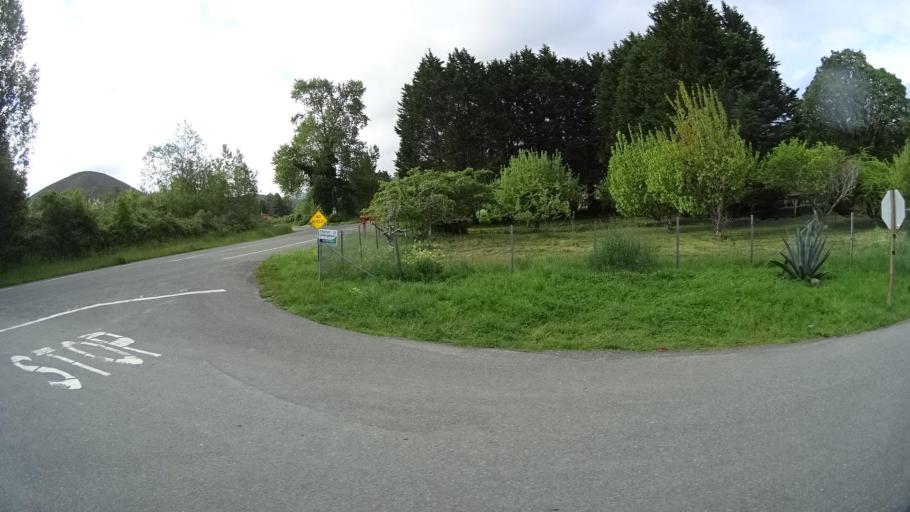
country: US
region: California
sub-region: Humboldt County
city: Blue Lake
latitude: 40.8682
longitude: -123.9959
